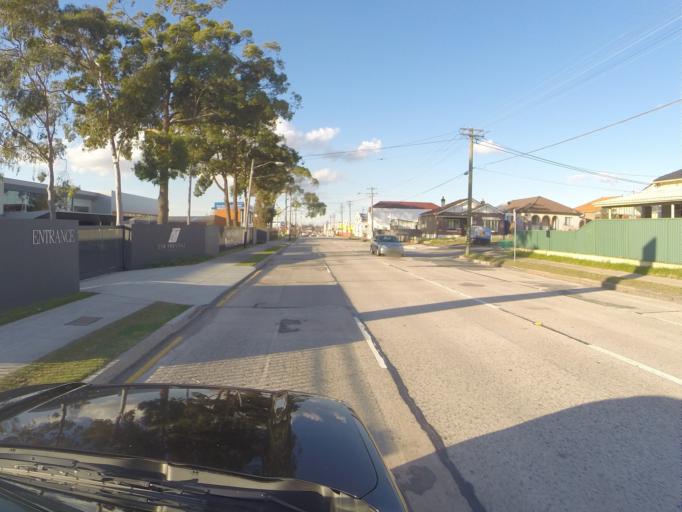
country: AU
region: New South Wales
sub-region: Canterbury
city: Canterbury
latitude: -33.9170
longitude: 151.1072
